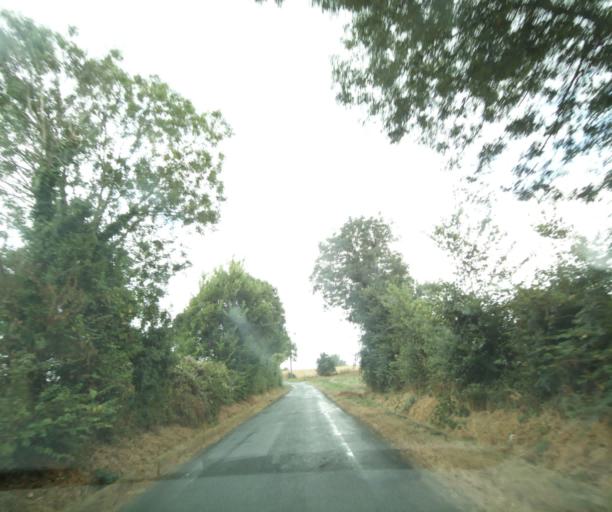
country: FR
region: Poitou-Charentes
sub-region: Departement de la Charente-Maritime
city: Tonnay-Charente
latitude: 45.9431
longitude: -0.8725
